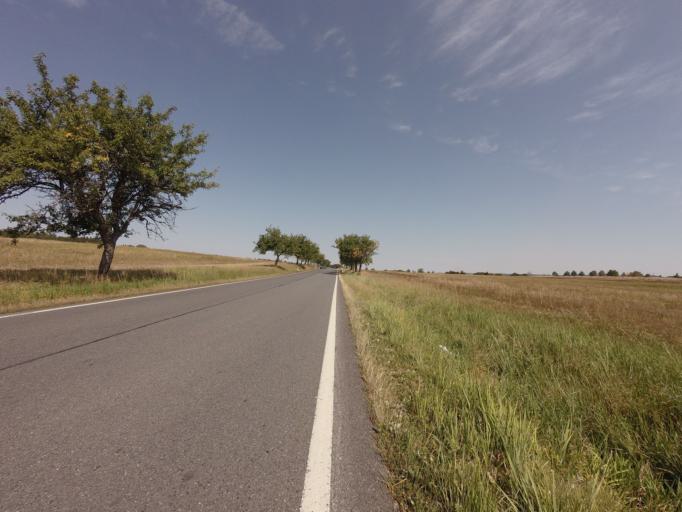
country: CZ
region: Jihocesky
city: Milevsko
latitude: 49.4315
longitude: 14.3593
